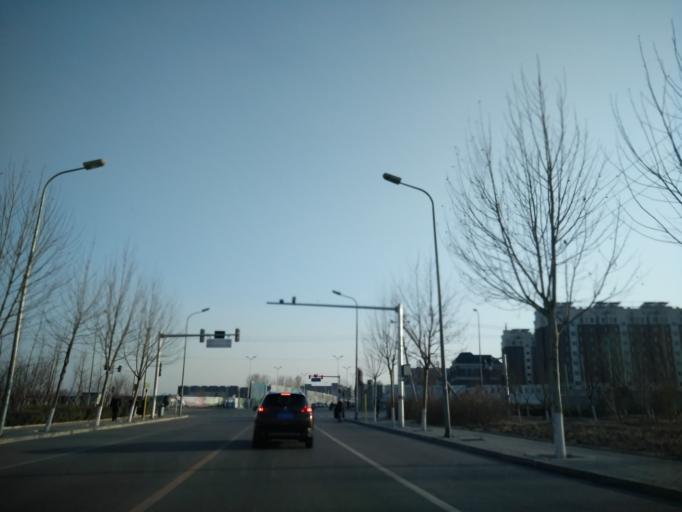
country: CN
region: Beijing
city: Yinghai
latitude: 39.7091
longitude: 116.3979
